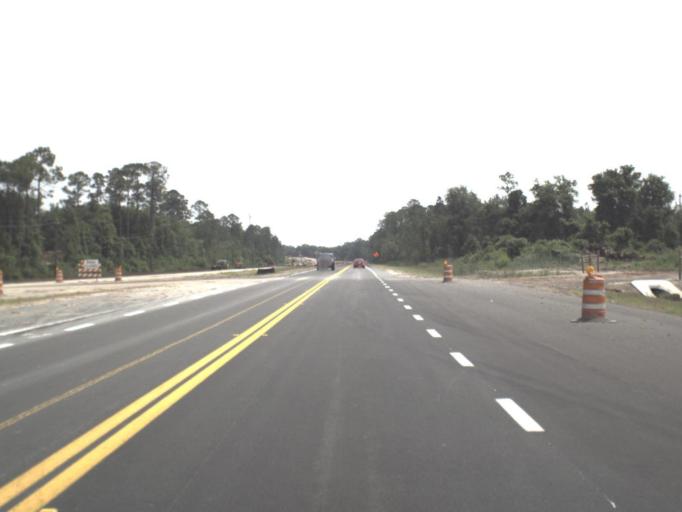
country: US
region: Florida
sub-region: Nassau County
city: Nassau Village-Ratliff
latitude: 30.4971
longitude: -81.8852
